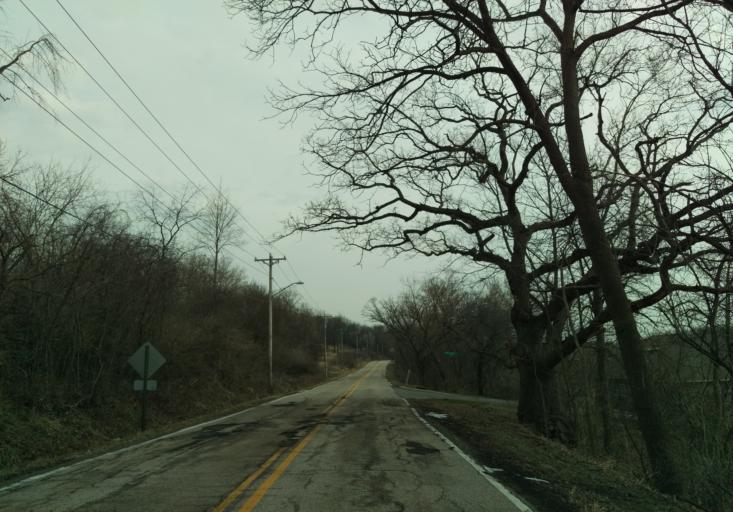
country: US
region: Wisconsin
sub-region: Dane County
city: Middleton
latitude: 43.1084
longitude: -89.4943
